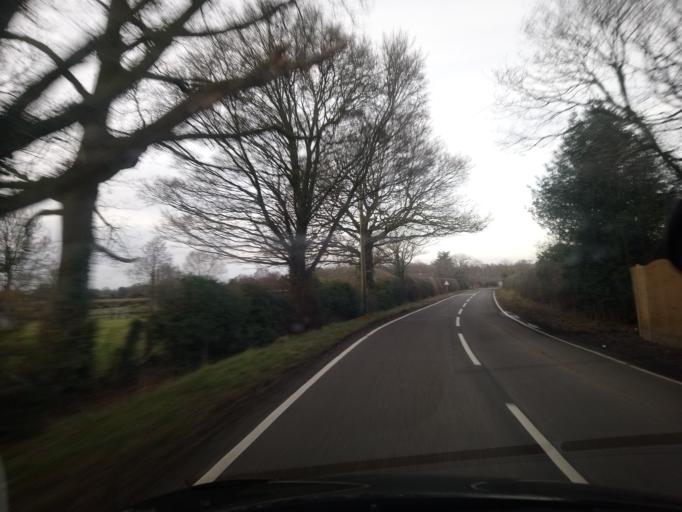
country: GB
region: England
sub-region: Shropshire
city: Prees
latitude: 52.9198
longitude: -2.6826
